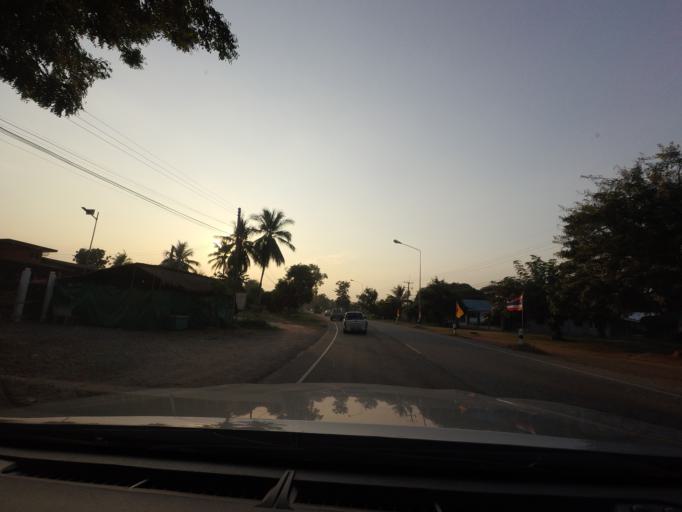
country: TH
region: Phitsanulok
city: Wang Thong
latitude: 16.7059
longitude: 100.5027
